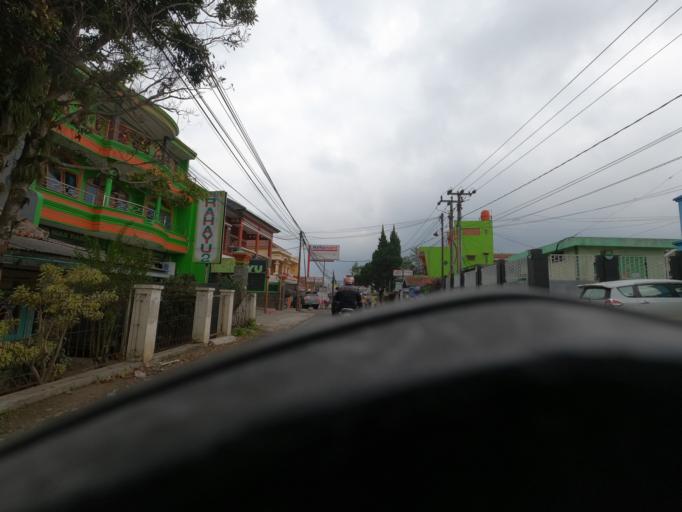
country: ID
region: West Java
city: Lembang
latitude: -6.8110
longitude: 107.5615
